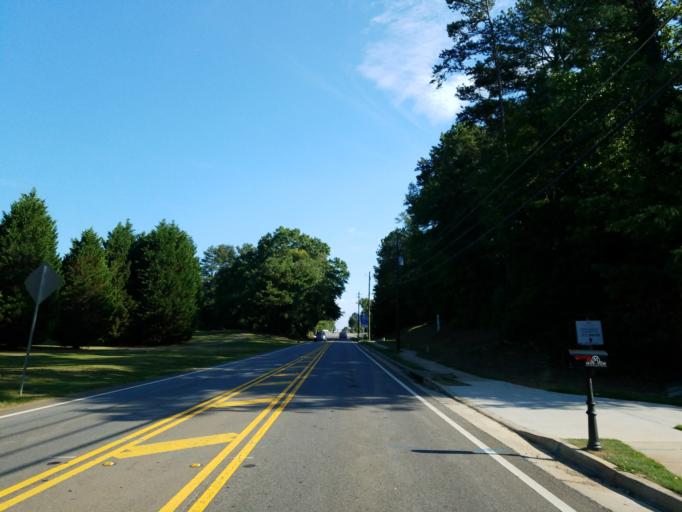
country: US
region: Georgia
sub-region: Fulton County
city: Alpharetta
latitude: 34.0957
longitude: -84.3394
